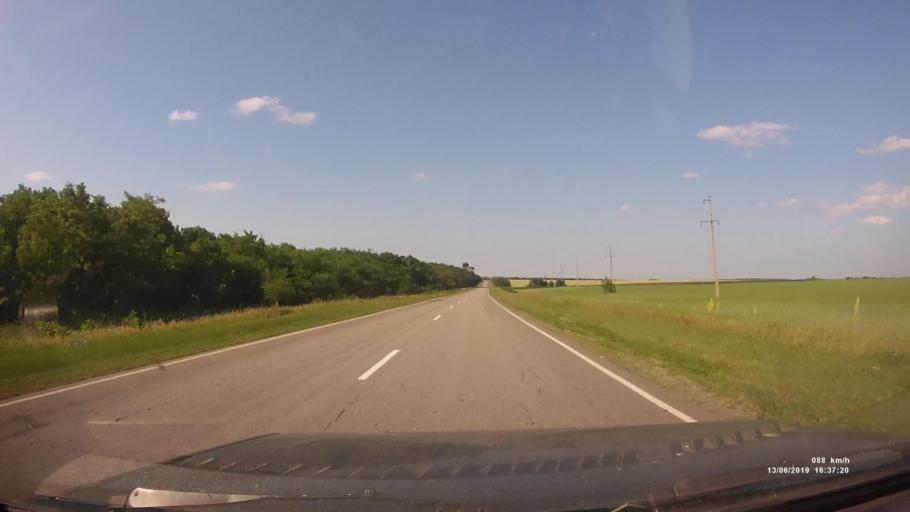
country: RU
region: Rostov
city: Kazanskaya
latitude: 49.9059
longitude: 41.3121
